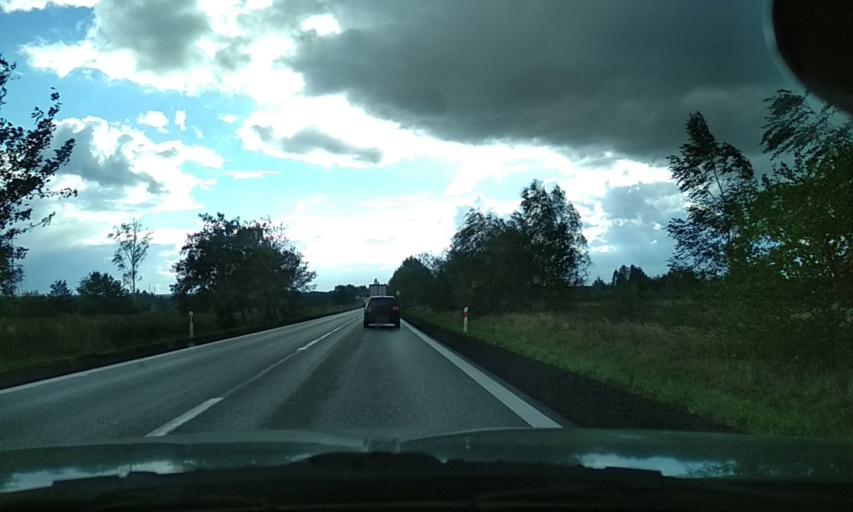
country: PL
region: Silesian Voivodeship
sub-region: Powiat gliwicki
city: Zernica
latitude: 50.2298
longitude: 18.6230
